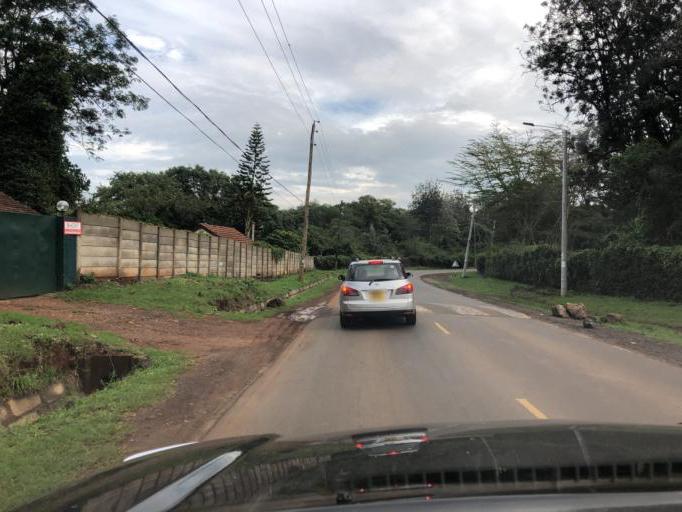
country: KE
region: Kajiado
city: Ngong
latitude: -1.3423
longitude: 36.7145
